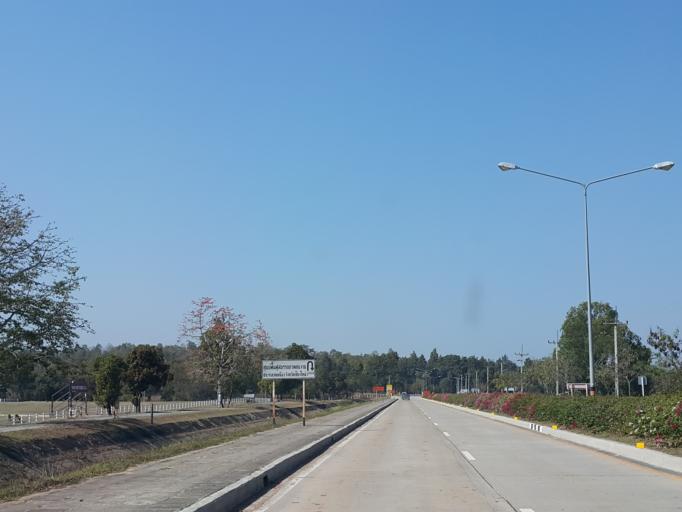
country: TH
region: Chiang Mai
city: Chiang Mai
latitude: 18.8612
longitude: 98.9605
